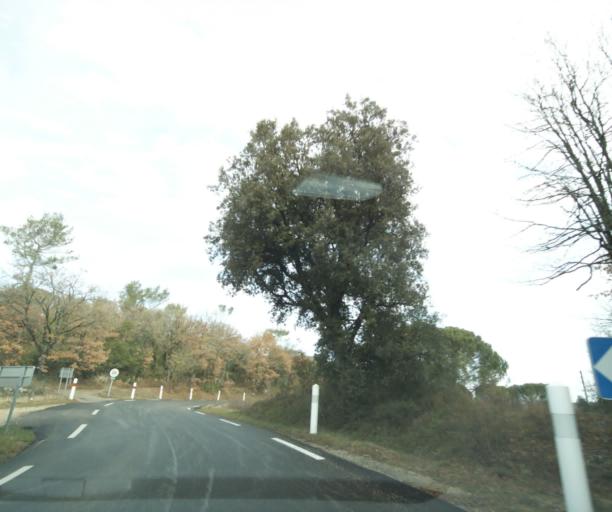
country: FR
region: Provence-Alpes-Cote d'Azur
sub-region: Departement du Var
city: Tourves
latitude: 43.4186
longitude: 5.9276
